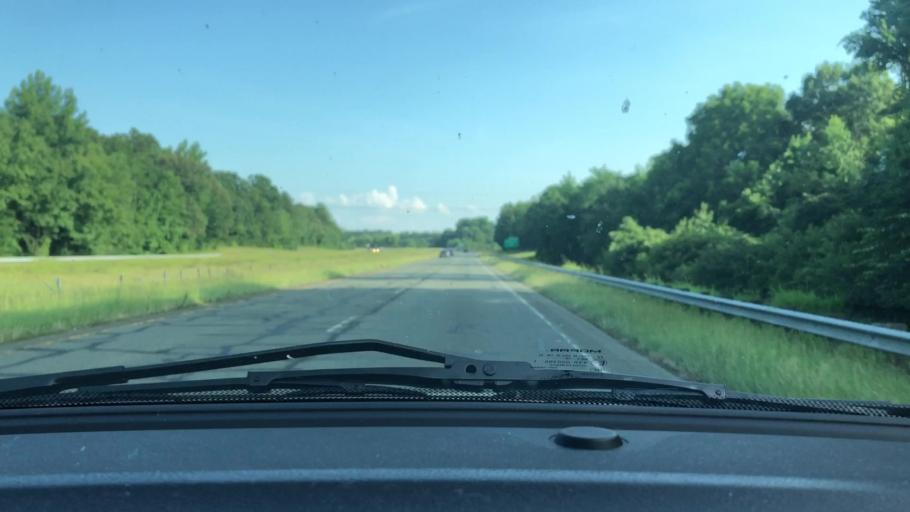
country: US
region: North Carolina
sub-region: Chatham County
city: Siler City
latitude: 35.7008
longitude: -79.4290
